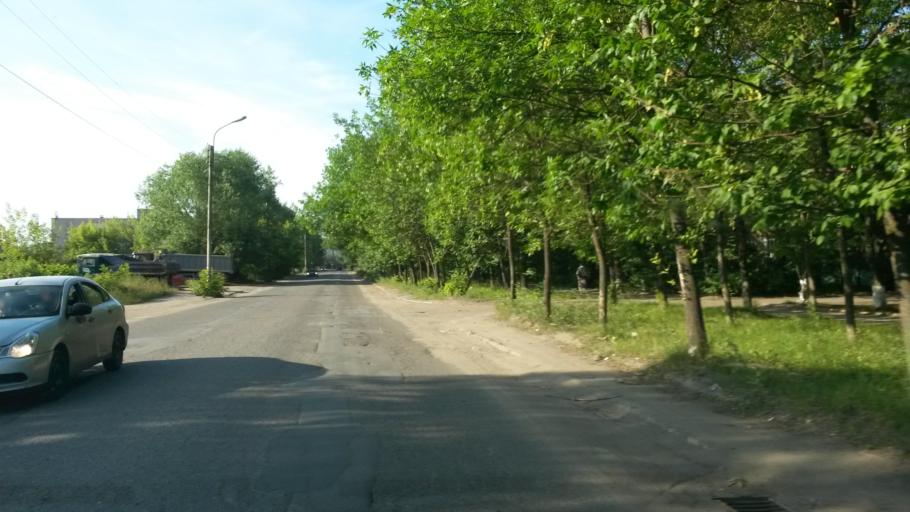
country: RU
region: Ivanovo
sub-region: Gorod Ivanovo
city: Ivanovo
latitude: 56.9597
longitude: 40.9851
